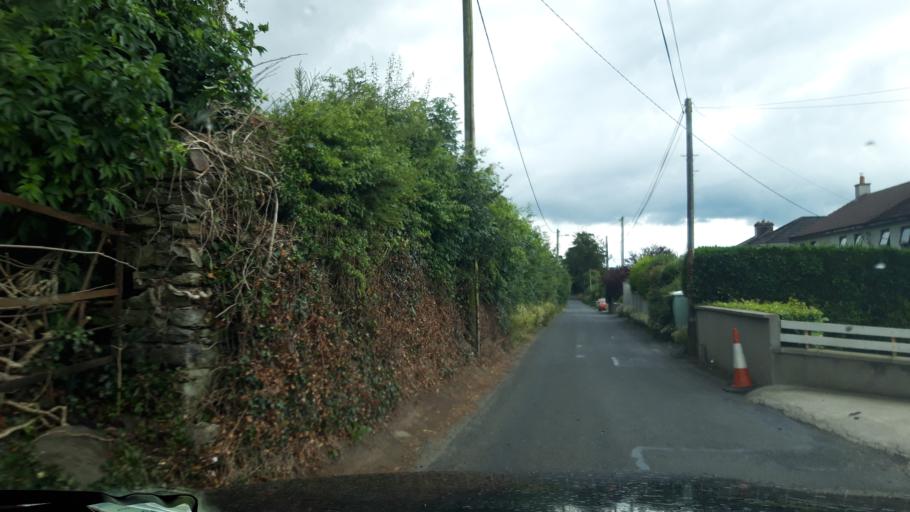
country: IE
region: Leinster
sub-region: Wicklow
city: Baltinglass
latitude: 52.9493
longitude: -6.7068
